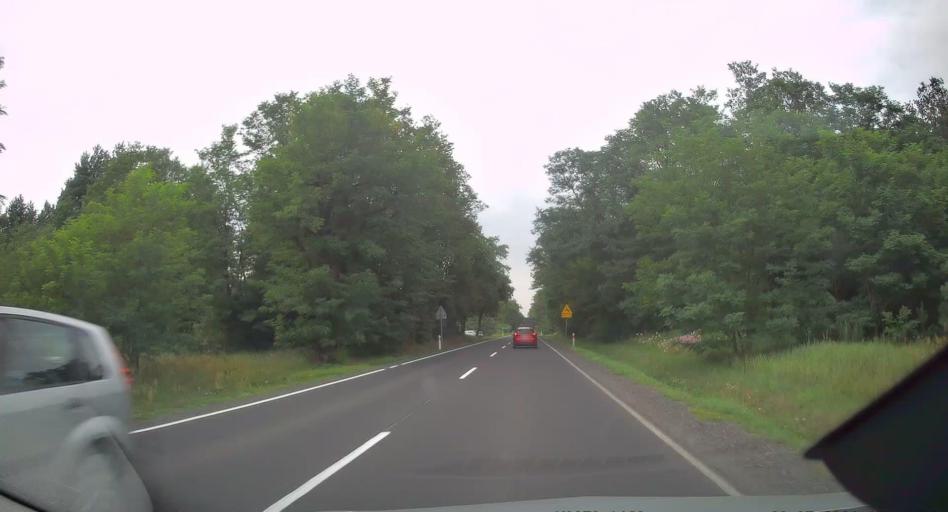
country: PL
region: Lodz Voivodeship
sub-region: Powiat radomszczanski
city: Gomunice
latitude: 51.1191
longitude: 19.4722
